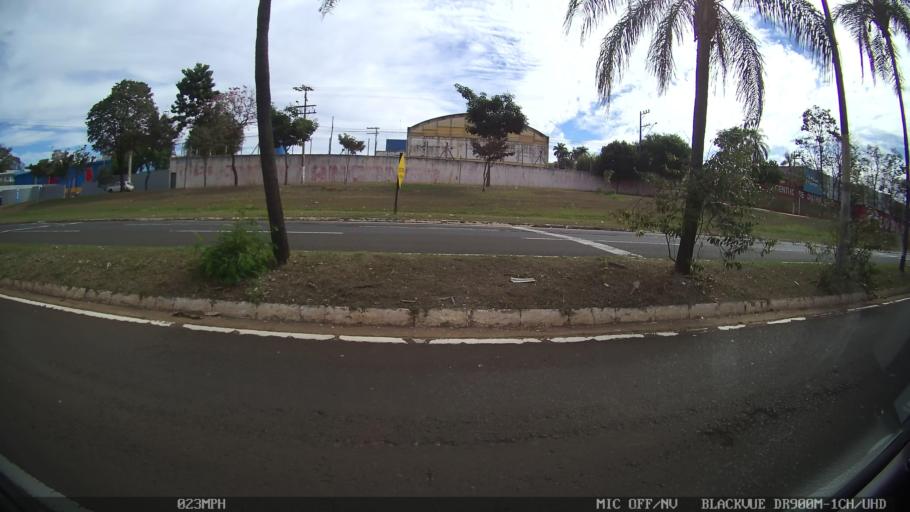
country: BR
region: Sao Paulo
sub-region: Catanduva
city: Catanduva
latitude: -21.1549
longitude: -48.9829
